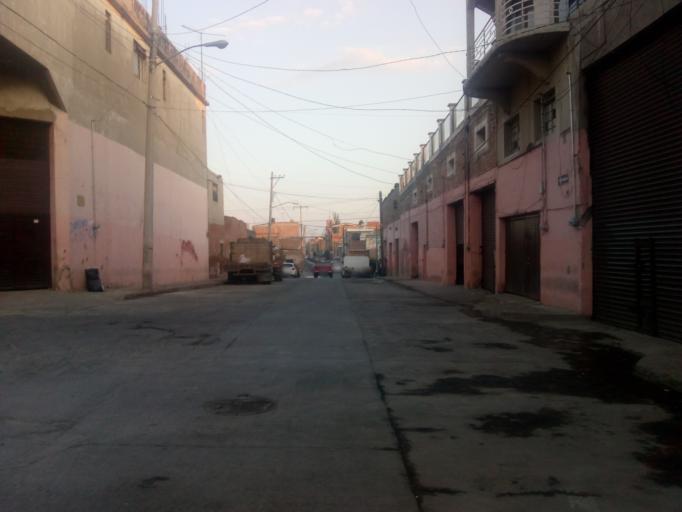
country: MX
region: Guanajuato
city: Leon
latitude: 21.1392
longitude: -101.6829
